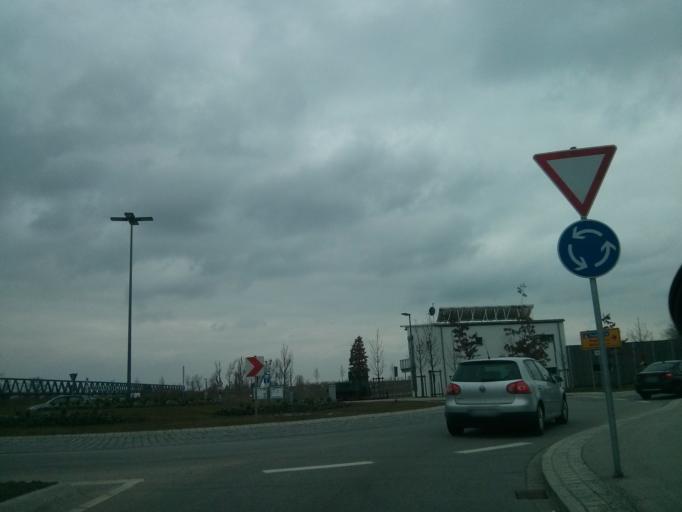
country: DE
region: Bavaria
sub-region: Lower Bavaria
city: Deggendorf
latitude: 48.8344
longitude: 12.9440
